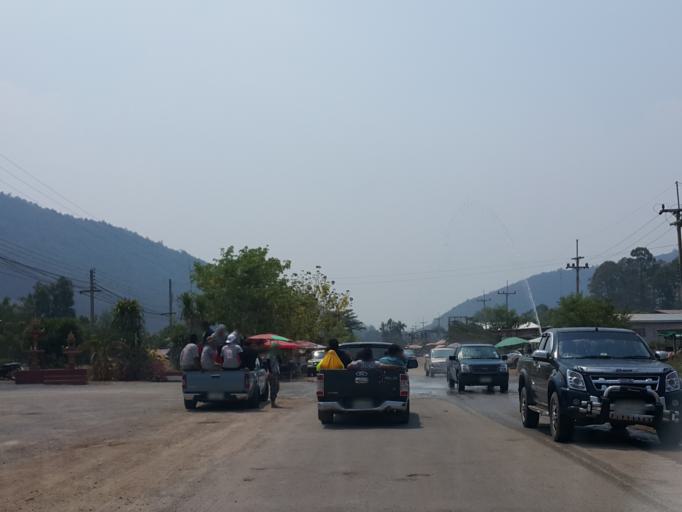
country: TH
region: Nakhon Sawan
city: Mae Wong
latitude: 15.8982
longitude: 99.4705
